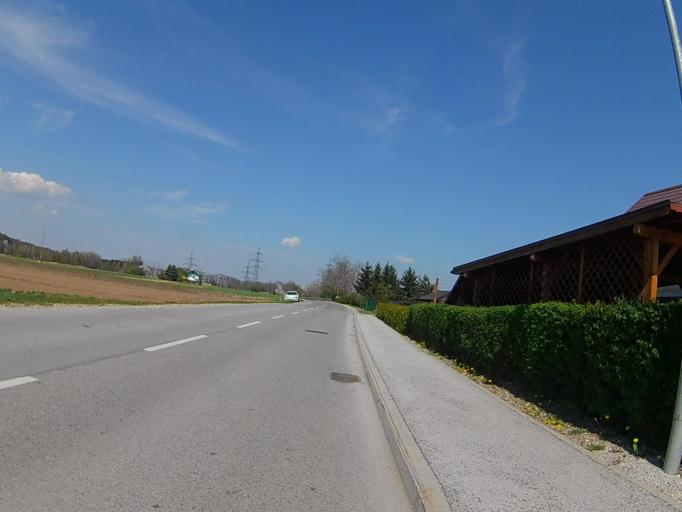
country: SI
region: Miklavz na Dravskem Polju
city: Miklavz na Dravskem Polju
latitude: 46.5136
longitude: 15.7004
